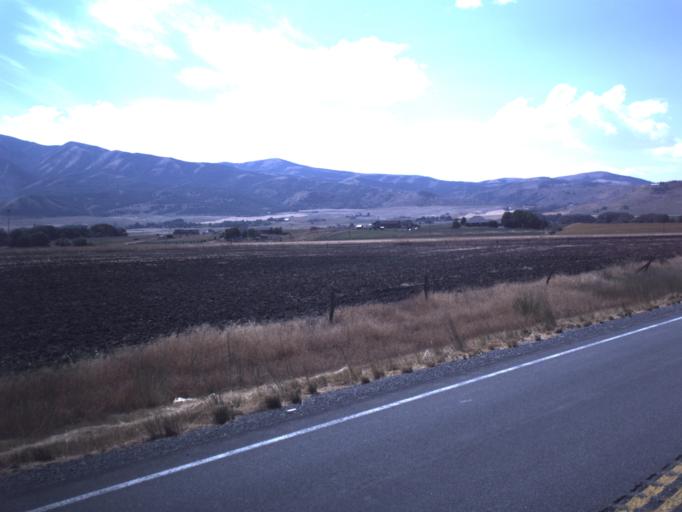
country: US
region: Utah
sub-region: Cache County
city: Mendon
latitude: 41.7490
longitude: -111.9717
